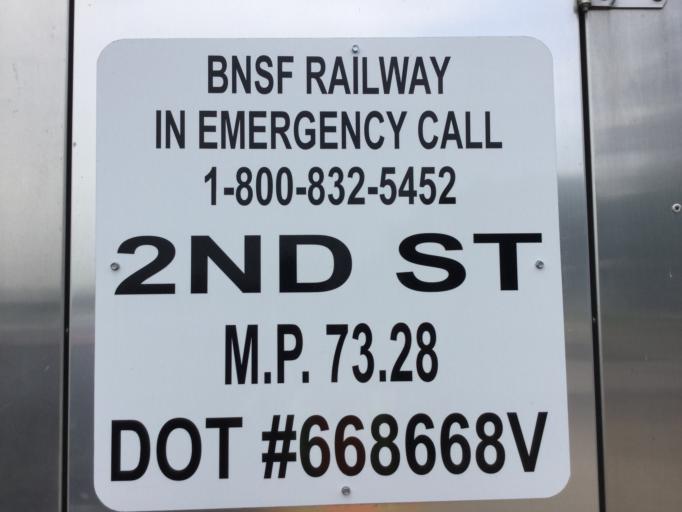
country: US
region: Kansas
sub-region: Linn County
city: Pleasanton
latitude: 38.1850
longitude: -94.7123
